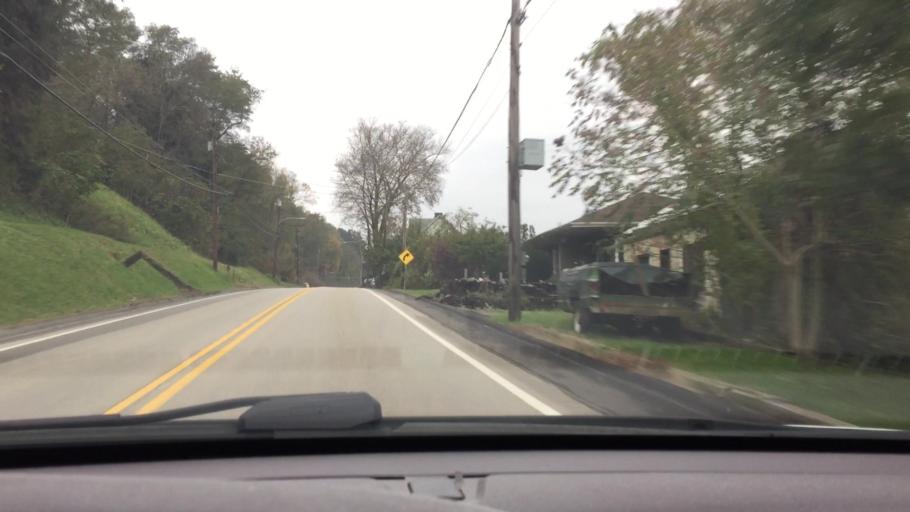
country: US
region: Pennsylvania
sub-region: Fayette County
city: Belle Vernon
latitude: 40.1161
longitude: -79.8634
